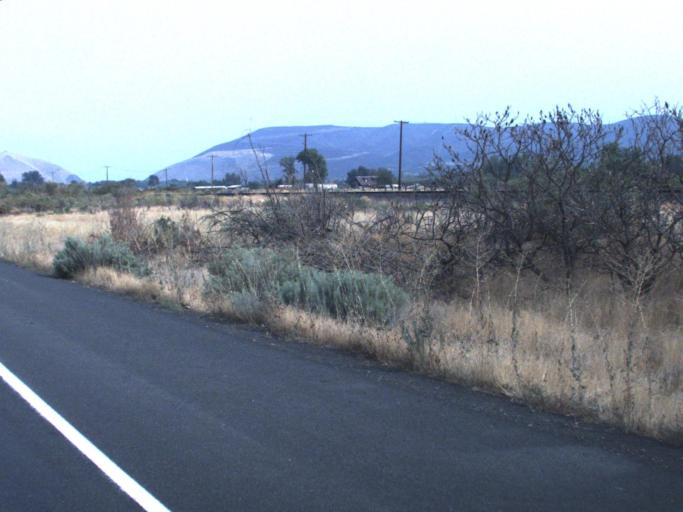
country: US
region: Washington
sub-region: Yakima County
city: Wapato
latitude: 46.4950
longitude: -120.4604
